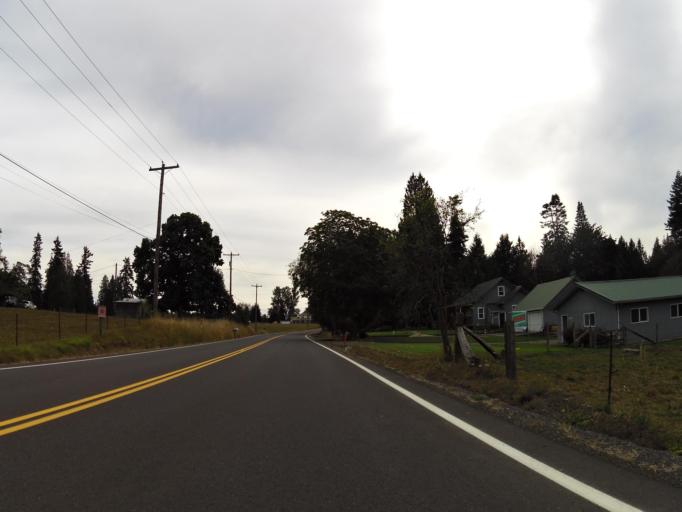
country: US
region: Washington
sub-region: Cowlitz County
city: Castle Rock
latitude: 46.2314
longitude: -122.8913
